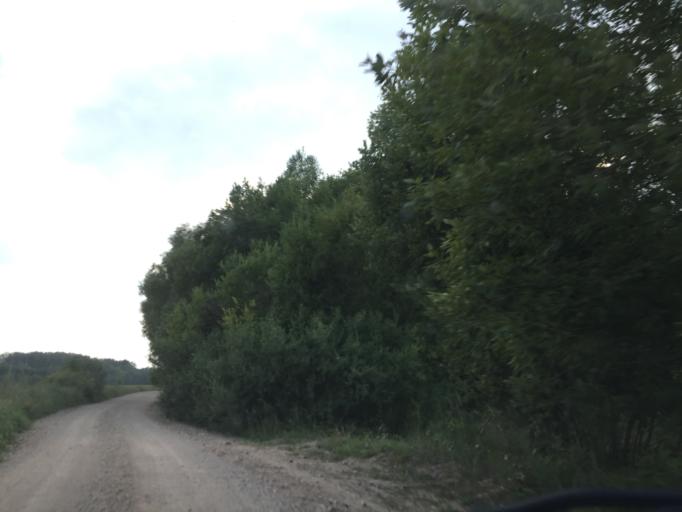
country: LT
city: Zagare
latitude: 56.4471
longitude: 23.1662
